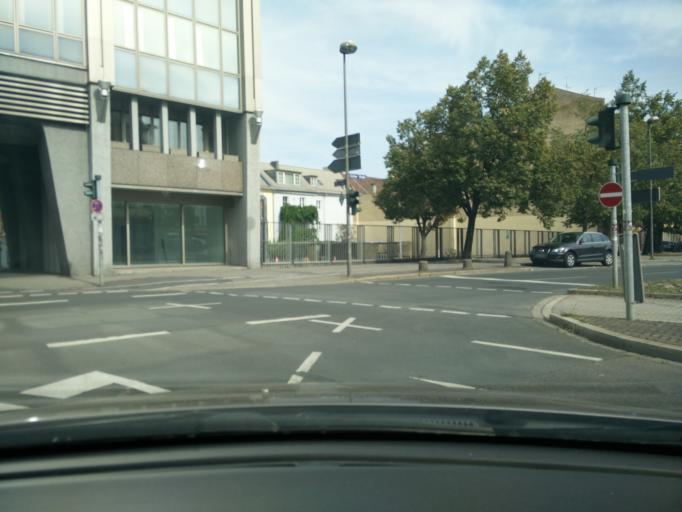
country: DE
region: Bavaria
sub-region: Regierungsbezirk Mittelfranken
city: Nuernberg
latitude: 49.4498
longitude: 11.0592
